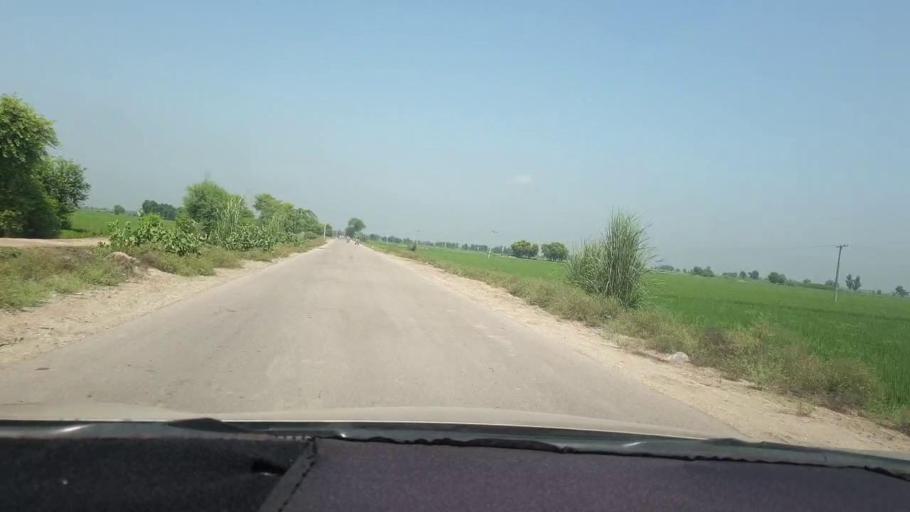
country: PK
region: Sindh
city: Miro Khan
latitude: 27.7631
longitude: 68.0752
